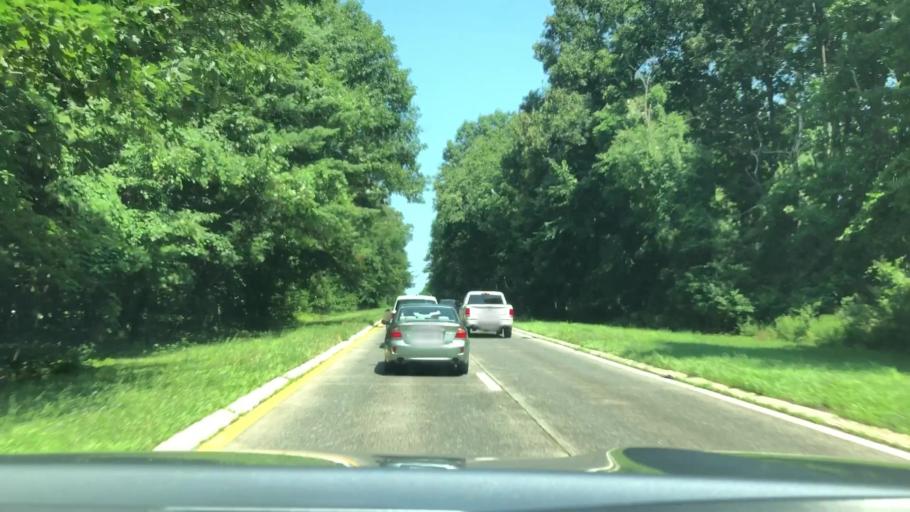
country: US
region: New York
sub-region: Rockland County
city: New Hempstead
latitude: 41.1551
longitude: -74.0266
